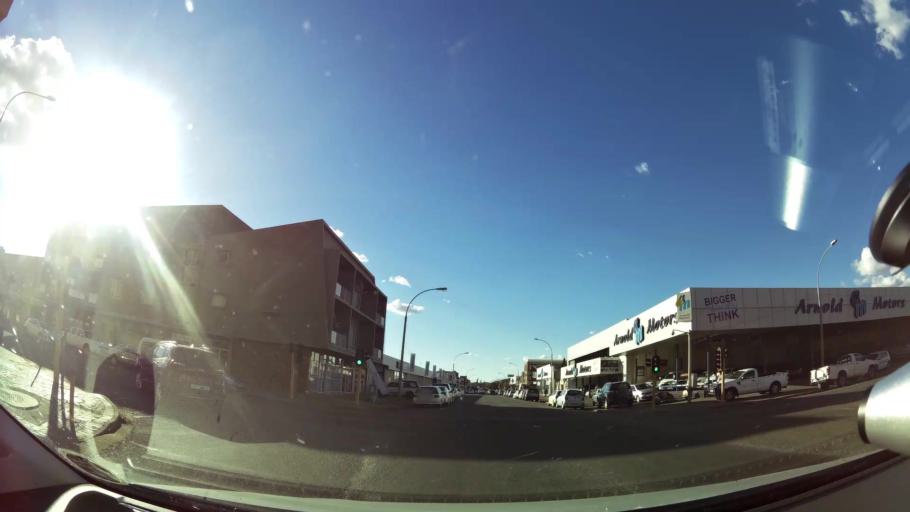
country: ZA
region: North-West
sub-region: Dr Kenneth Kaunda District Municipality
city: Klerksdorp
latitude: -26.8678
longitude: 26.6677
